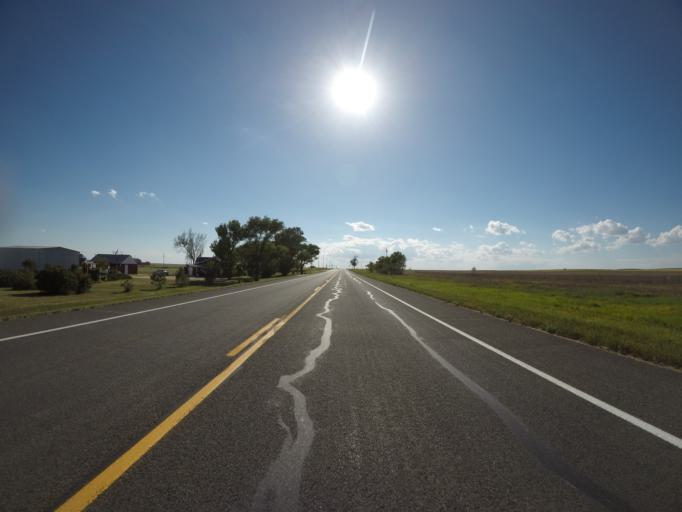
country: US
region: Colorado
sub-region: Morgan County
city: Brush
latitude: 40.6101
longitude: -103.6640
